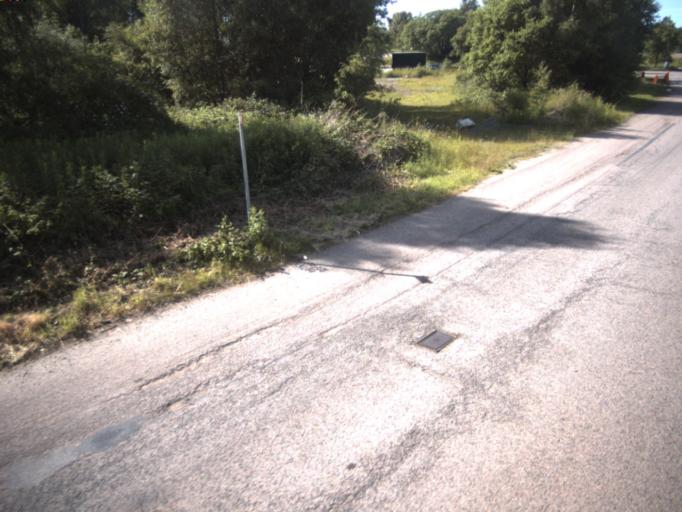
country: SE
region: Skane
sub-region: Helsingborg
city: Odakra
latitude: 56.0740
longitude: 12.7447
